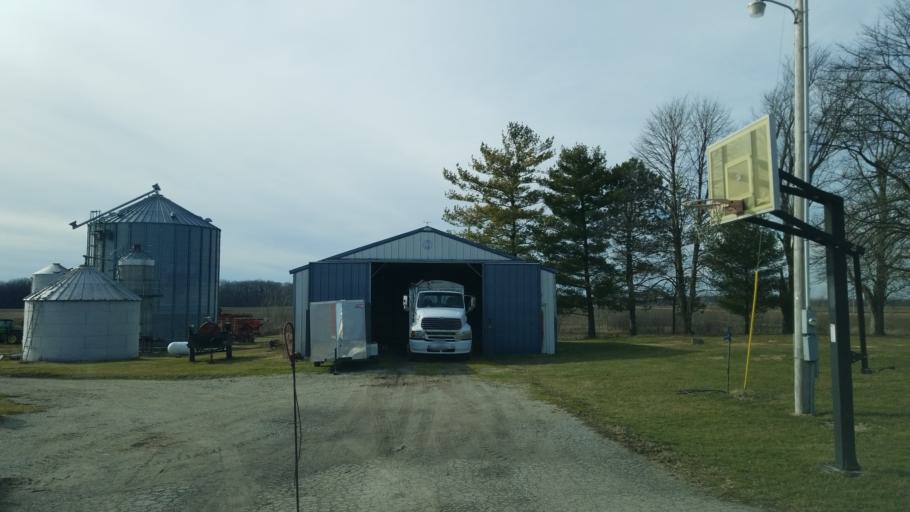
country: US
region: Ohio
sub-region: Wyandot County
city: Upper Sandusky
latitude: 40.6565
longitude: -83.3245
